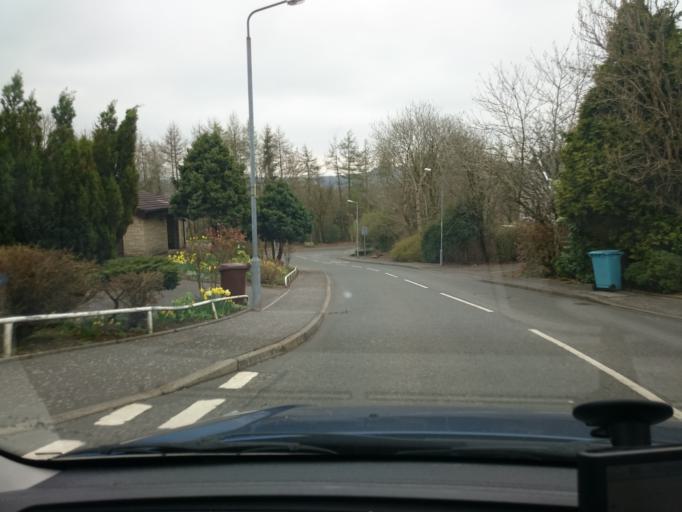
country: GB
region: Scotland
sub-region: North Lanarkshire
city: Kilsyth
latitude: 55.9823
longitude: -4.0582
